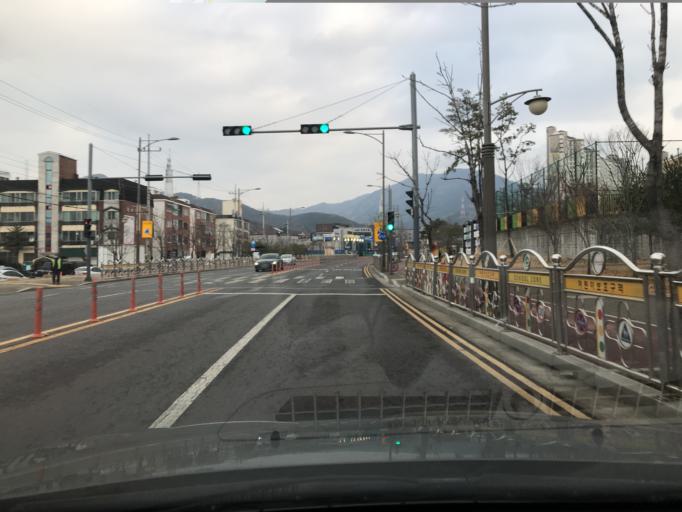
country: KR
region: Daegu
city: Hwawon
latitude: 35.6947
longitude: 128.4509
